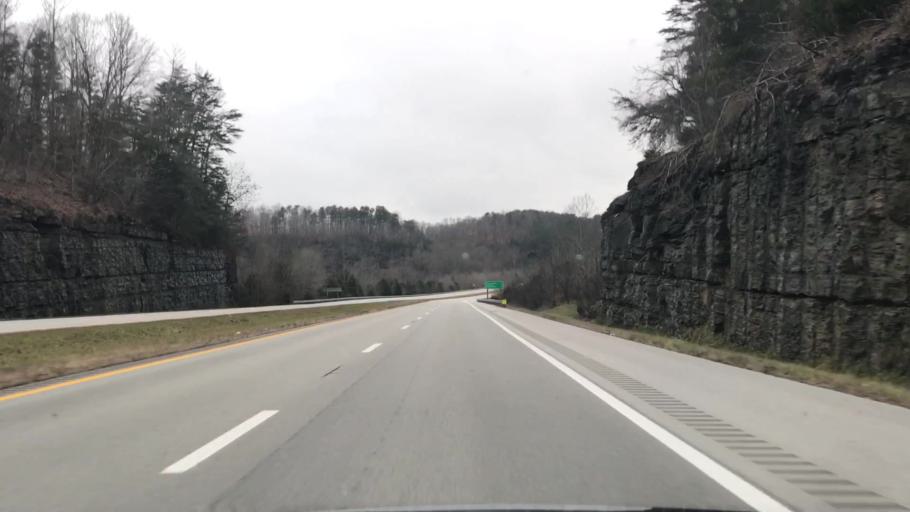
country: US
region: Kentucky
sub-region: Russell County
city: Russell Springs
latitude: 37.0901
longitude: -84.8832
